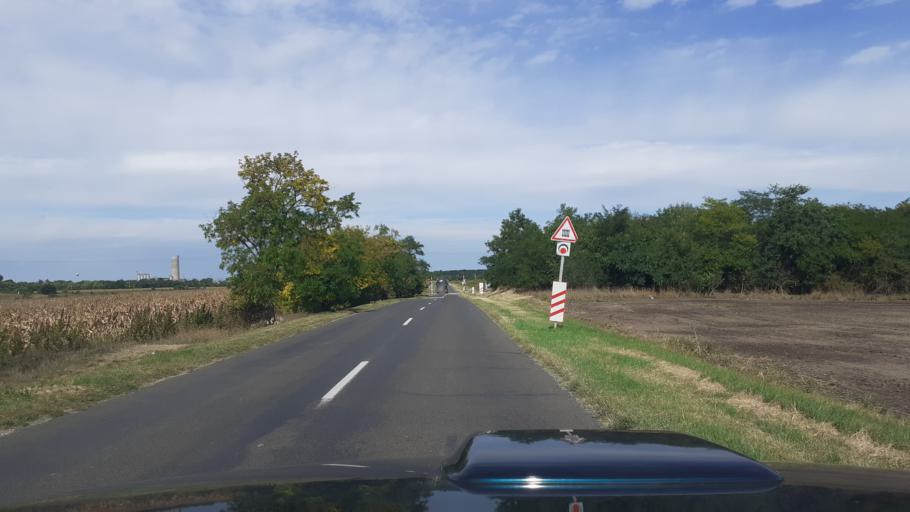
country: HU
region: Fejer
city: Pusztaszabolcs
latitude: 47.1236
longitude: 18.6870
